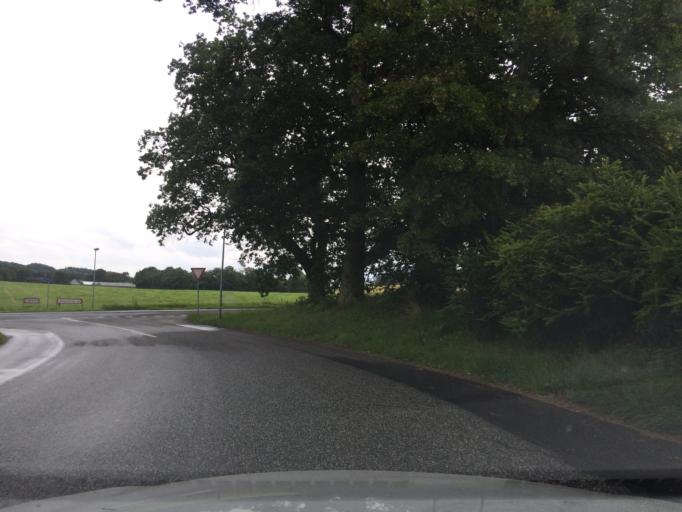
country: DK
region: Central Jutland
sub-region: Skanderborg Kommune
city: Ry
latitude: 56.2155
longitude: 9.7425
